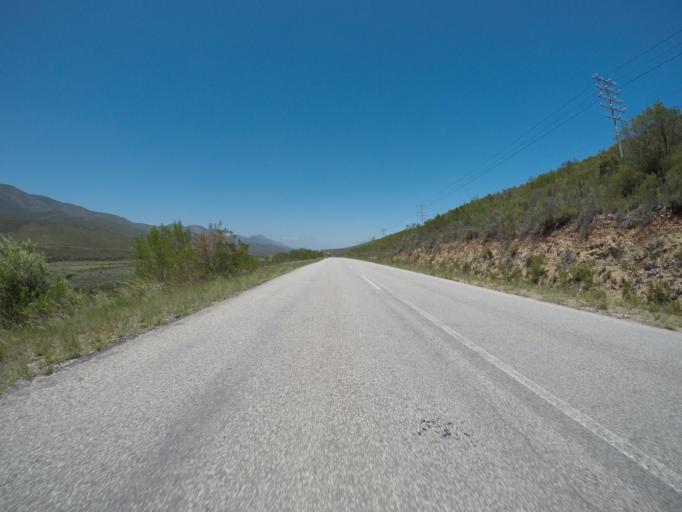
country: ZA
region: Eastern Cape
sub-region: Cacadu District Municipality
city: Kareedouw
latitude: -33.8810
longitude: 24.0604
